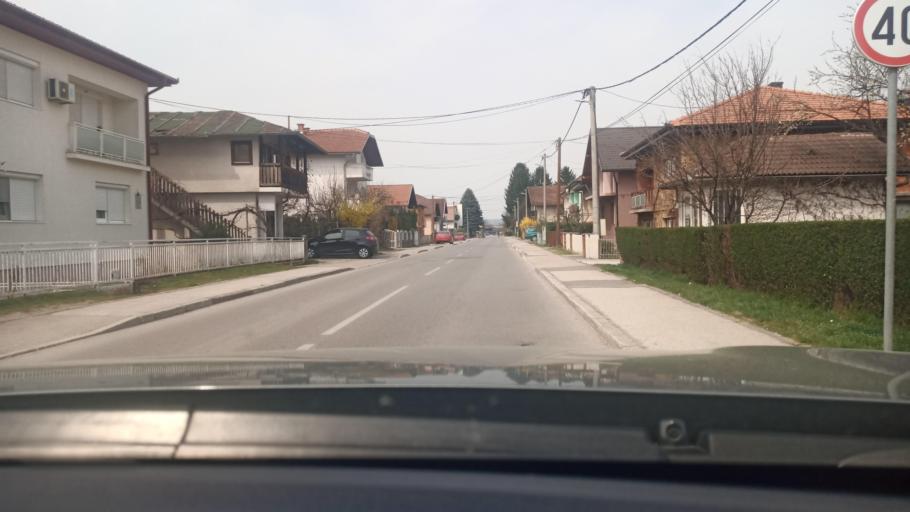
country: BA
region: Federation of Bosnia and Herzegovina
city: Bihac
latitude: 44.8188
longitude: 15.8677
